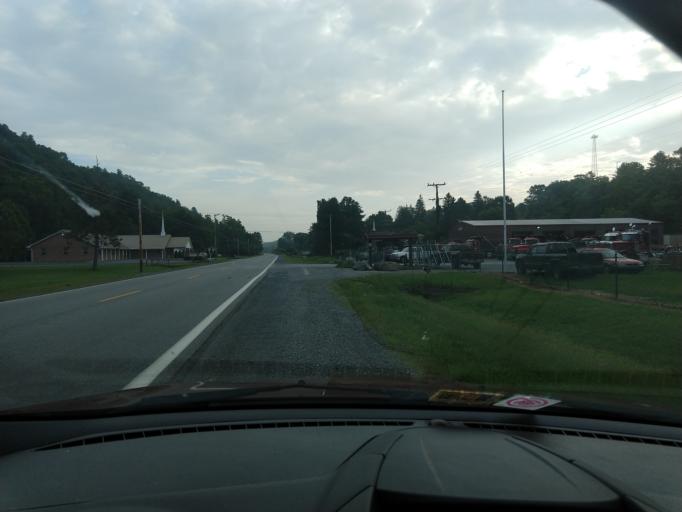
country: US
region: West Virginia
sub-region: Greenbrier County
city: White Sulphur Springs
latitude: 37.8315
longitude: -80.2602
